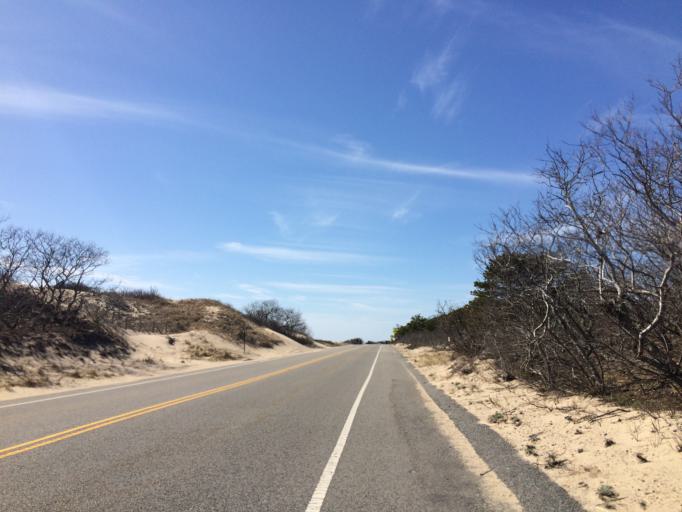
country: US
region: Massachusetts
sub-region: Barnstable County
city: Provincetown
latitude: 42.0411
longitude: -70.2098
